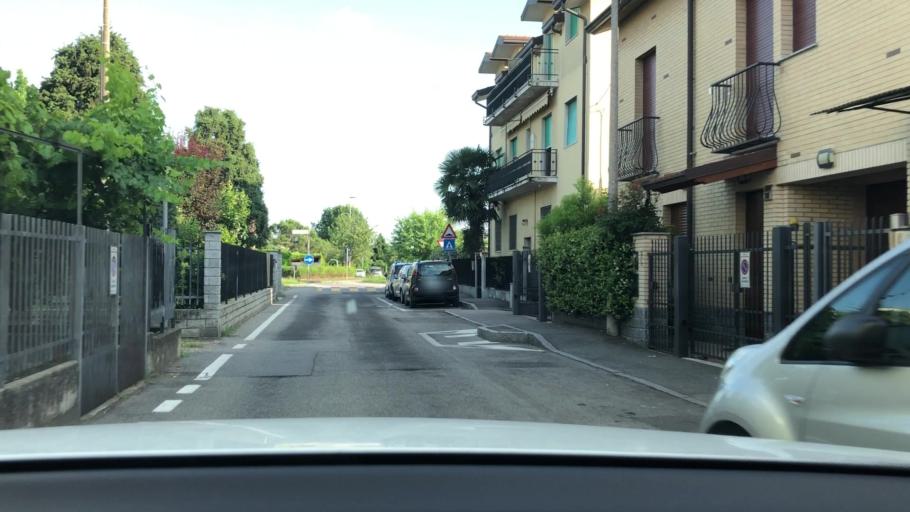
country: IT
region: Lombardy
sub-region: Citta metropolitana di Milano
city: Cusano Milanino
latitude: 45.5676
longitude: 9.1853
